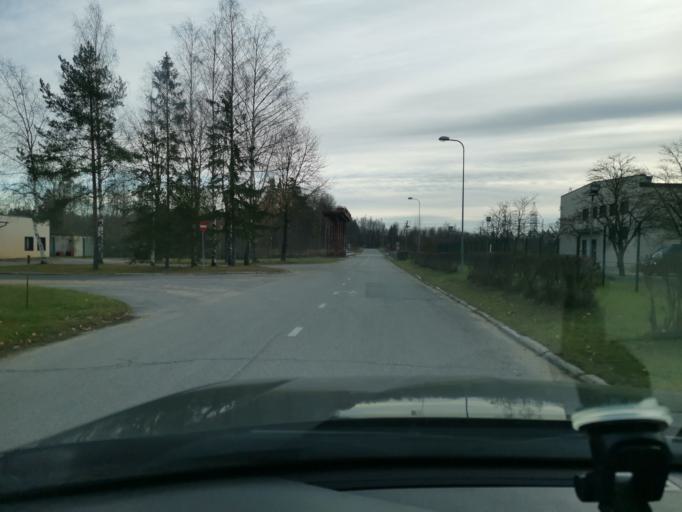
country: EE
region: Ida-Virumaa
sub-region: Sillamaee linn
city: Sillamae
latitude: 59.2735
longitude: 27.9113
